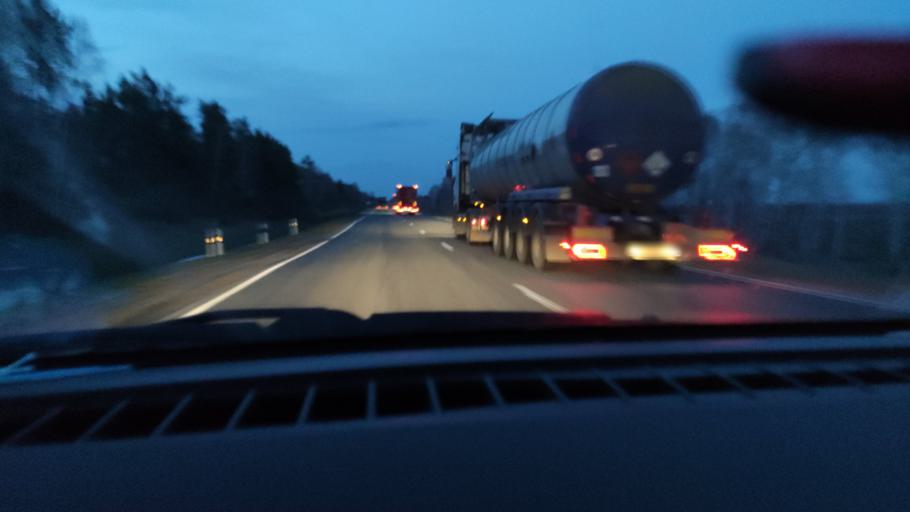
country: RU
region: Saratov
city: Sennoy
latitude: 52.1081
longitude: 46.8253
